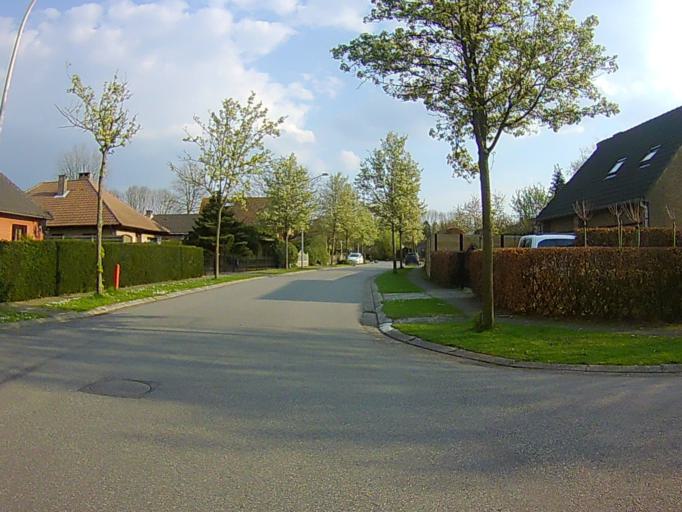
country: BE
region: Flanders
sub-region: Provincie Antwerpen
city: Kalmthout
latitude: 51.3811
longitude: 4.4704
